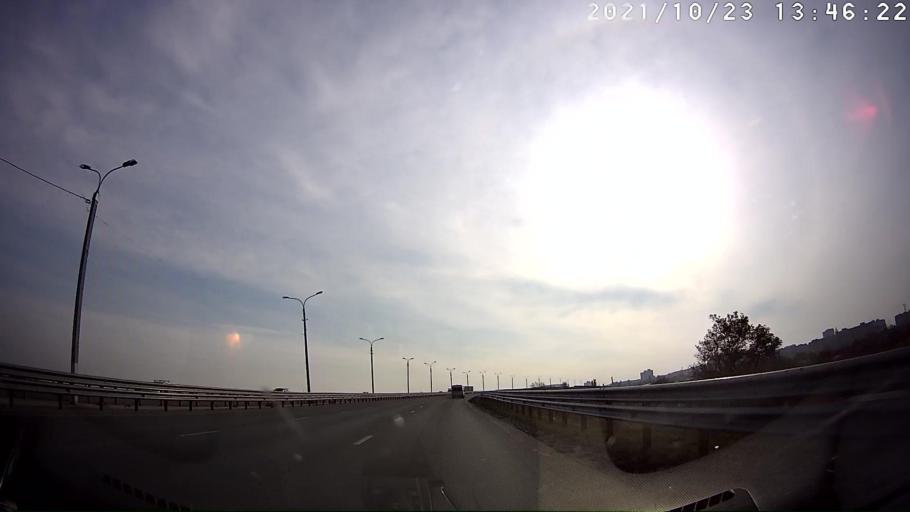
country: RU
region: Volgograd
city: Volgograd
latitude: 48.7708
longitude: 44.5192
